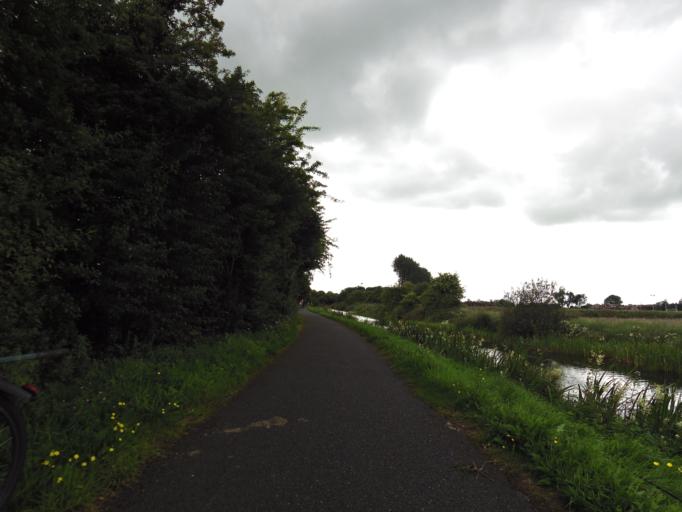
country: IE
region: Leinster
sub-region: An Iarmhi
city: An Muileann gCearr
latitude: 53.5102
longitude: -7.3997
